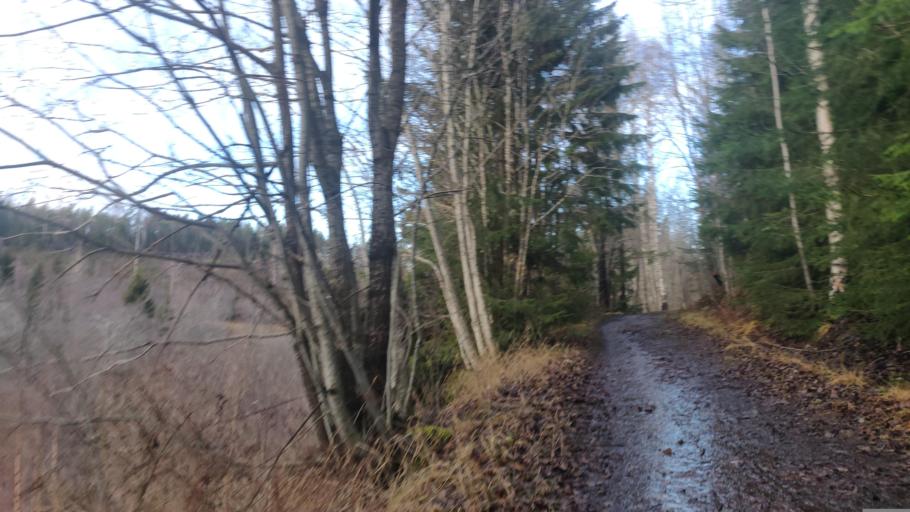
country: SE
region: Vaesternorrland
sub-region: Sundsvalls Kommun
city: Nolby
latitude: 62.3010
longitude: 17.3565
